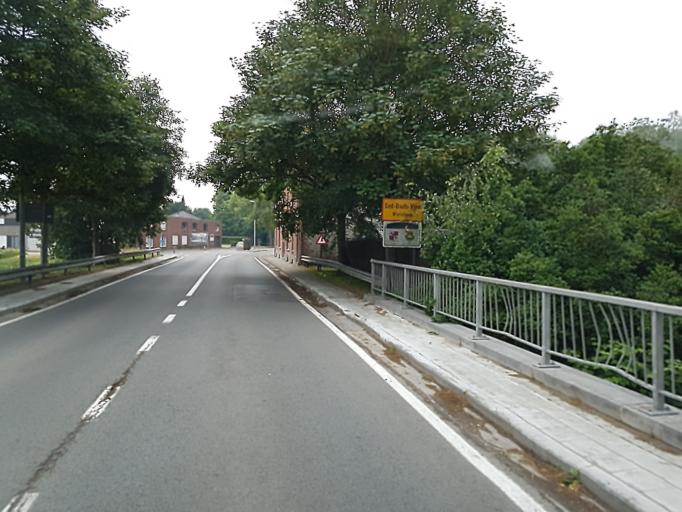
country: BE
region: Flanders
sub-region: Provincie West-Vlaanderen
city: Dentergem
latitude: 50.9282
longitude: 3.3973
